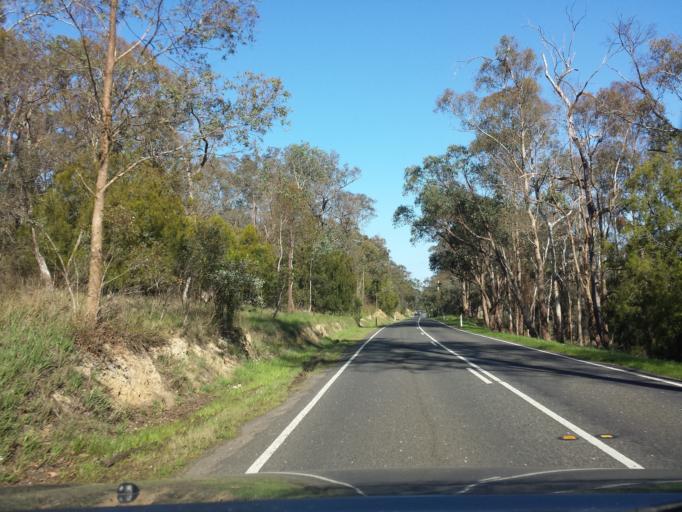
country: AU
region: Victoria
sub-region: Yarra Ranges
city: Yarra Glen
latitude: -37.6487
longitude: 145.3277
